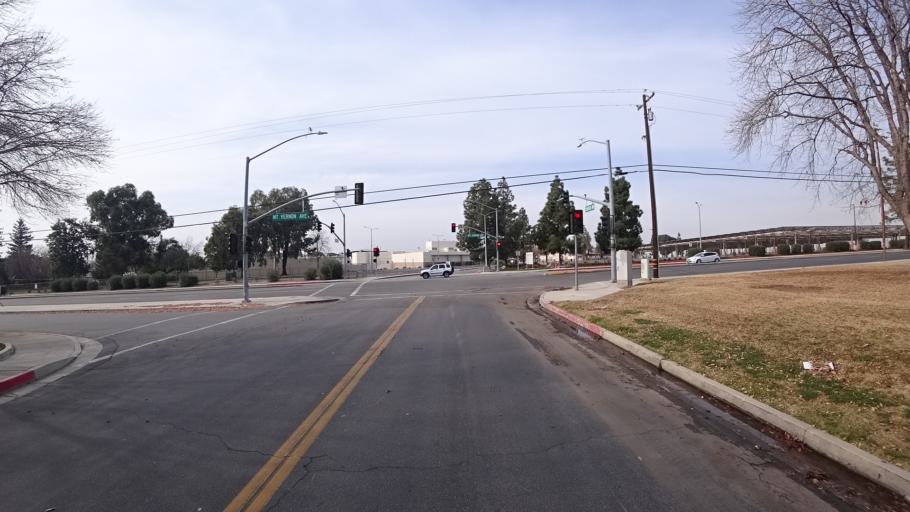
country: US
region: California
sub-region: Kern County
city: Oildale
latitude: 35.4106
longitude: -118.9672
